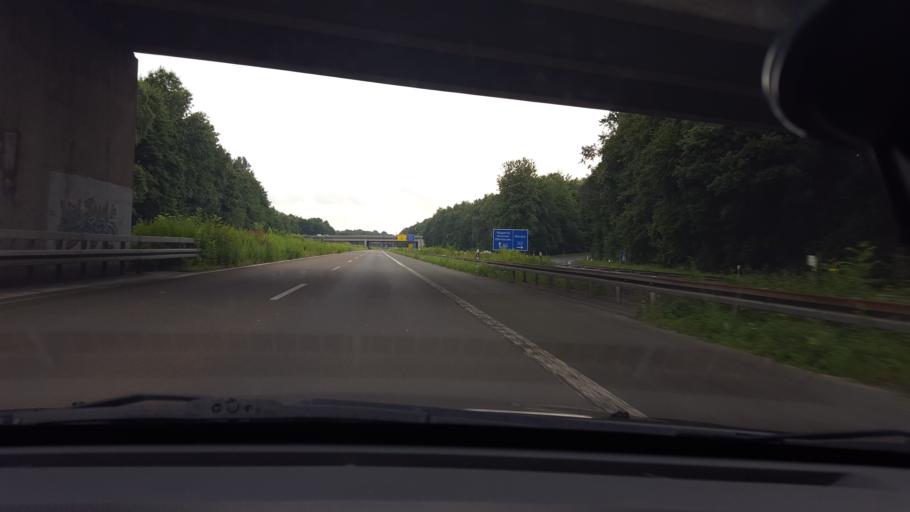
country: DE
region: North Rhine-Westphalia
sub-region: Regierungsbezirk Munster
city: Recklinghausen
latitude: 51.6229
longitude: 7.1718
